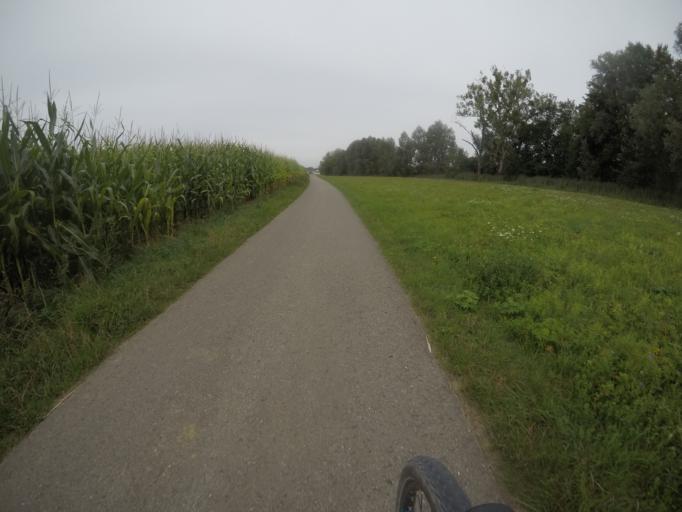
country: DE
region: Baden-Wuerttemberg
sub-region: Regierungsbezirk Stuttgart
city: Magstadt
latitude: 48.7428
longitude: 8.9836
